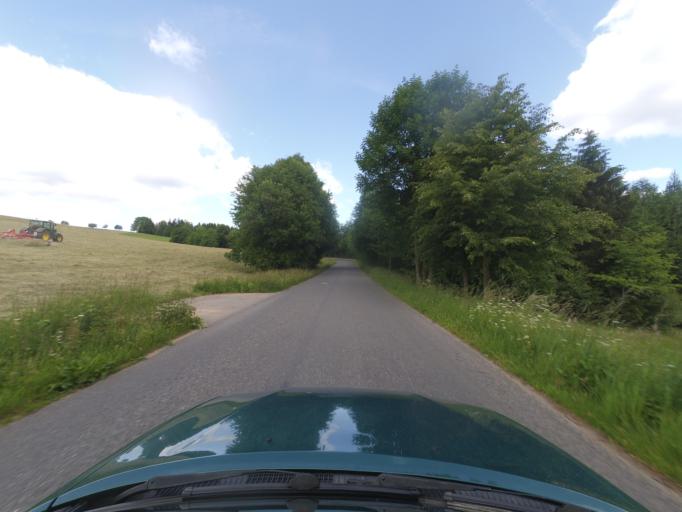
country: PL
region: Lower Silesian Voivodeship
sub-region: Powiat klodzki
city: Miedzylesie
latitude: 50.1176
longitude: 16.5877
